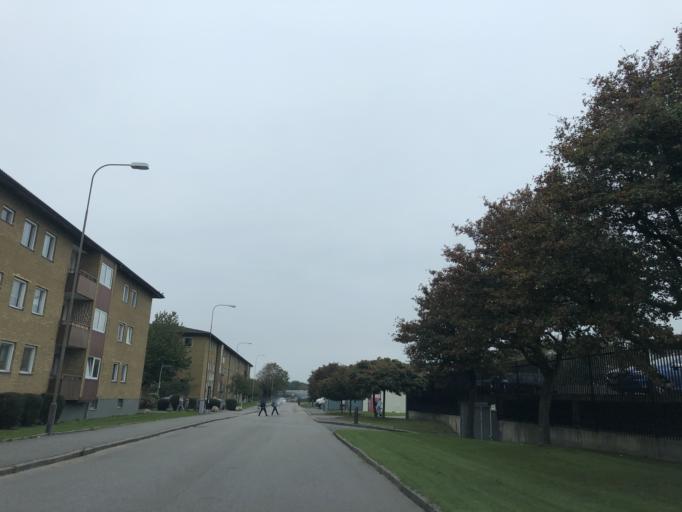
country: SE
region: Vaestra Goetaland
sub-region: Goteborg
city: Majorna
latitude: 57.6567
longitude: 11.8956
